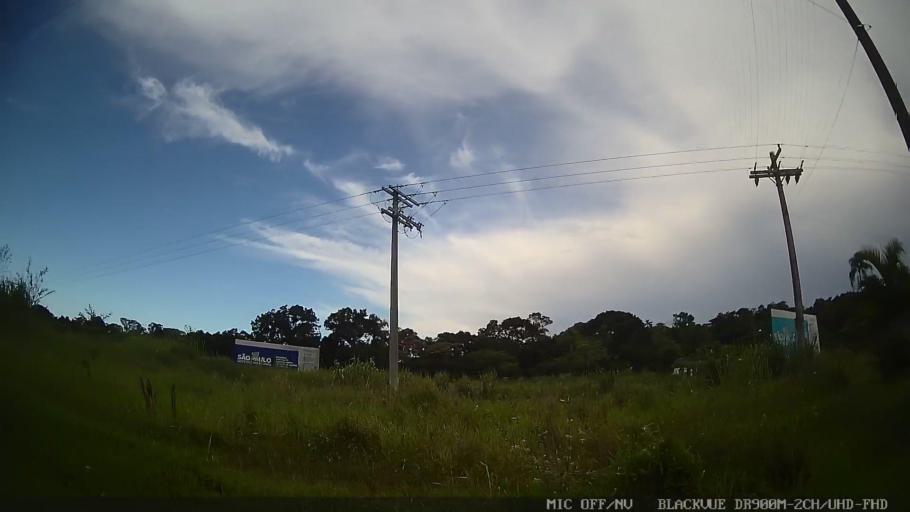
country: BR
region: Sao Paulo
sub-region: Iguape
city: Iguape
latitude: -24.6860
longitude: -47.4739
